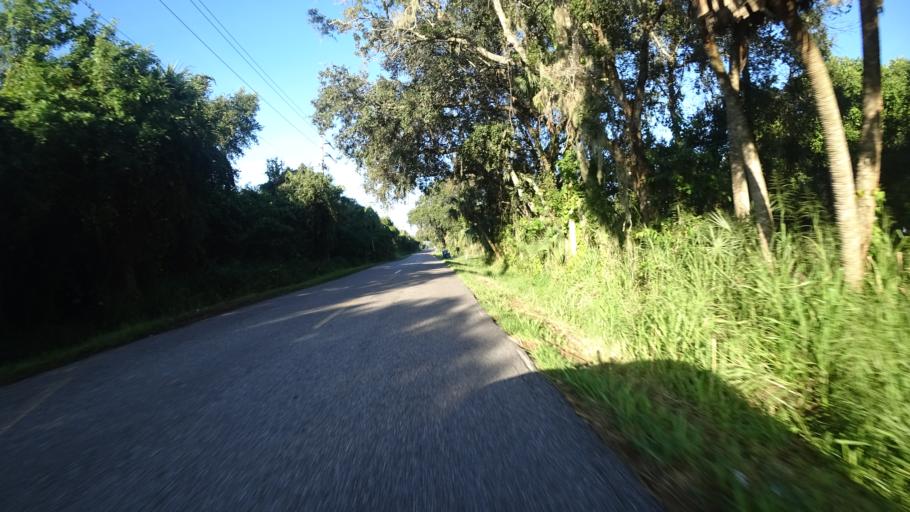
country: US
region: Florida
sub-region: Manatee County
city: Memphis
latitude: 27.5489
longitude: -82.5530
